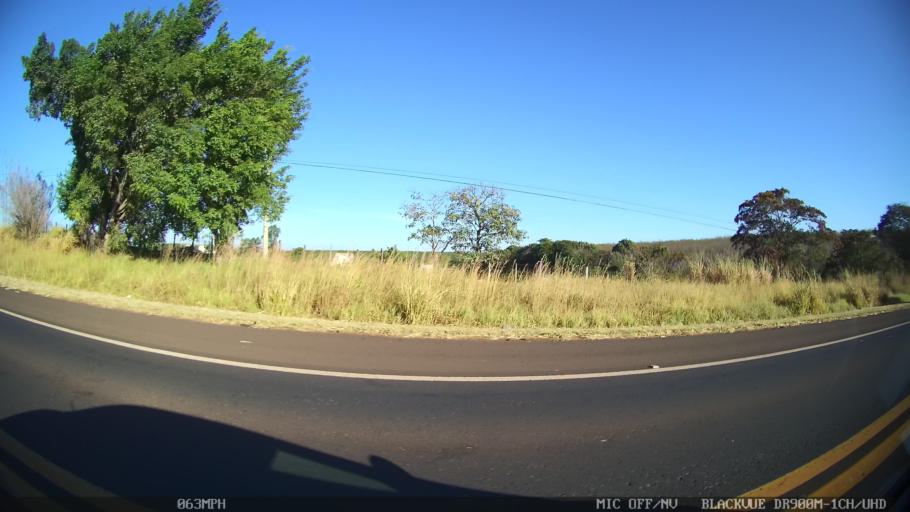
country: BR
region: Sao Paulo
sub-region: Olimpia
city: Olimpia
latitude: -20.7118
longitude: -48.9800
